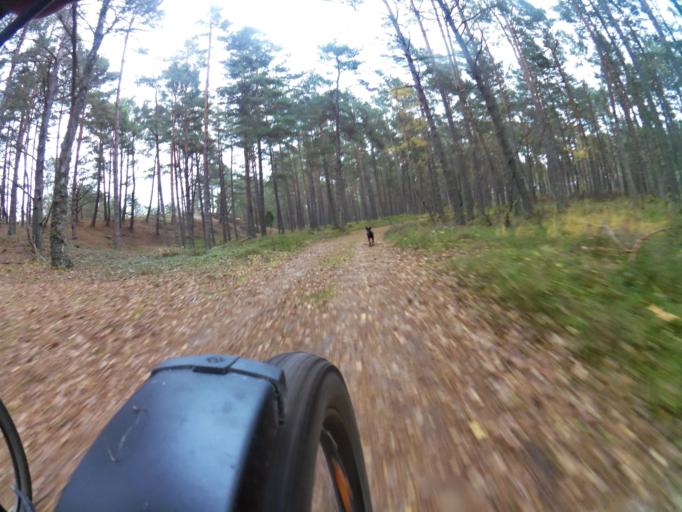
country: PL
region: Pomeranian Voivodeship
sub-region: Powiat leborski
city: Leba
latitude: 54.7782
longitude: 17.6989
